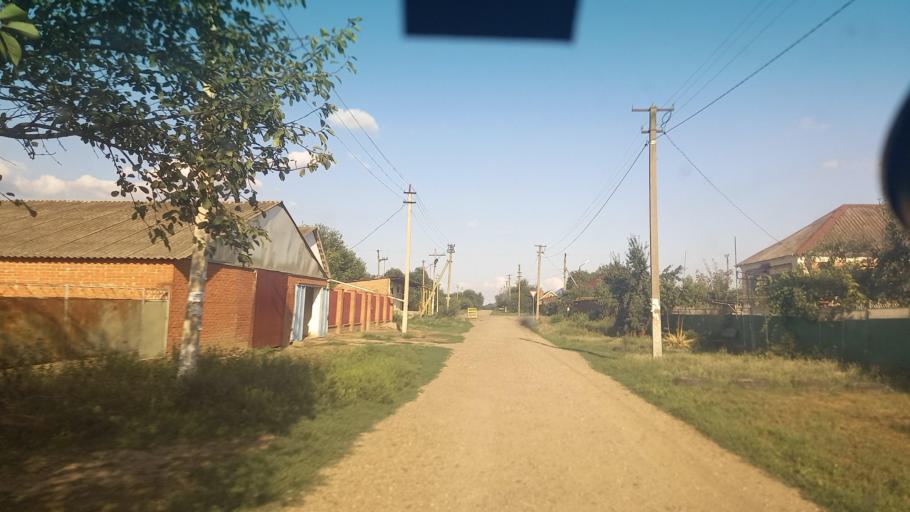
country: RU
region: Adygeya
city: Khatukay
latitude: 45.2975
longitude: 39.5635
